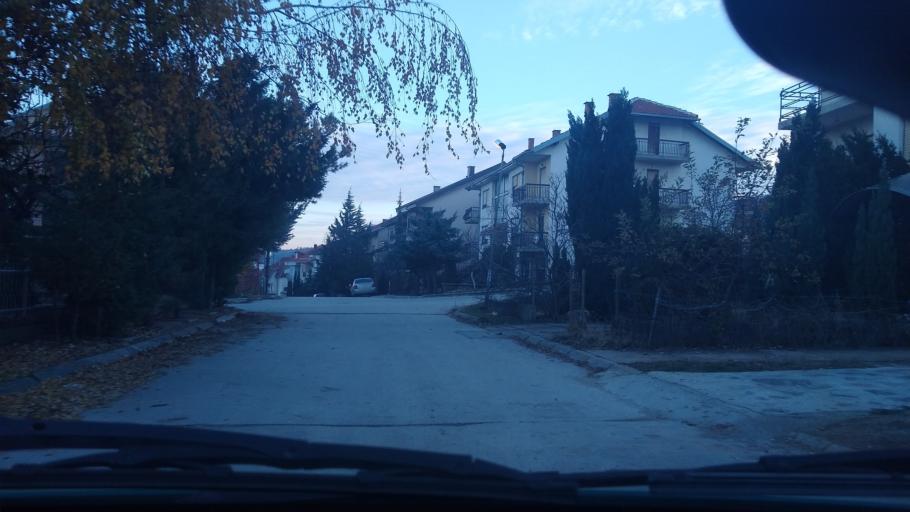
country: MK
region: Bitola
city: Bitola
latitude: 41.0247
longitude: 21.3057
